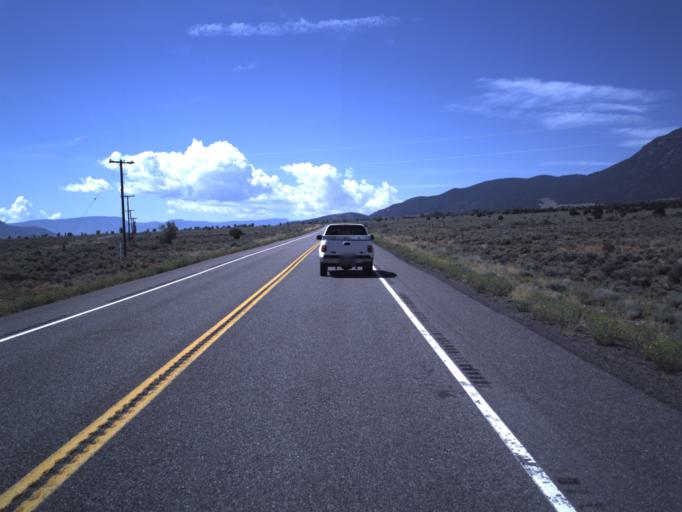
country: US
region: Utah
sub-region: Piute County
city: Junction
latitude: 38.4010
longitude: -112.2312
